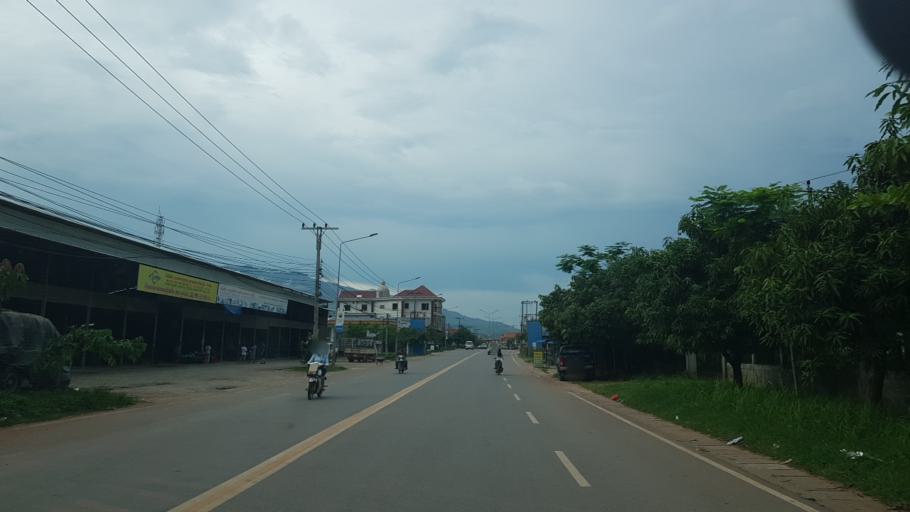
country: LA
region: Oudomxai
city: Muang Xay
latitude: 20.6742
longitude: 101.9848
